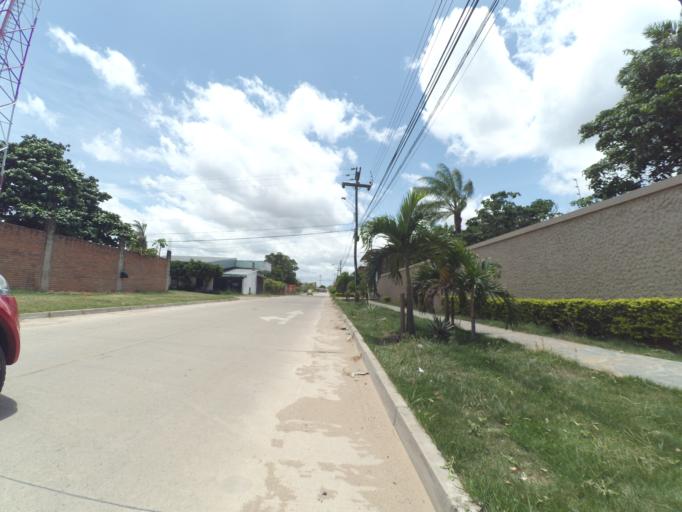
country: BO
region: Santa Cruz
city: Santa Cruz de la Sierra
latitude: -17.8106
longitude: -63.2131
